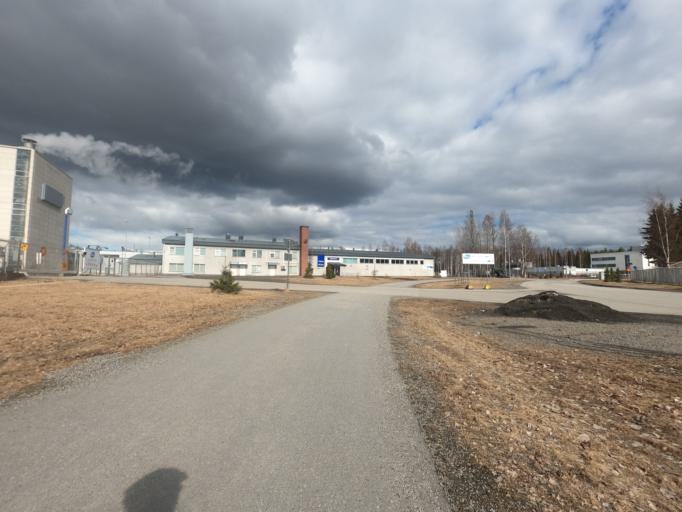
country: FI
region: North Karelia
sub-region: Joensuu
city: Joensuu
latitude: 62.6026
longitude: 29.7844
